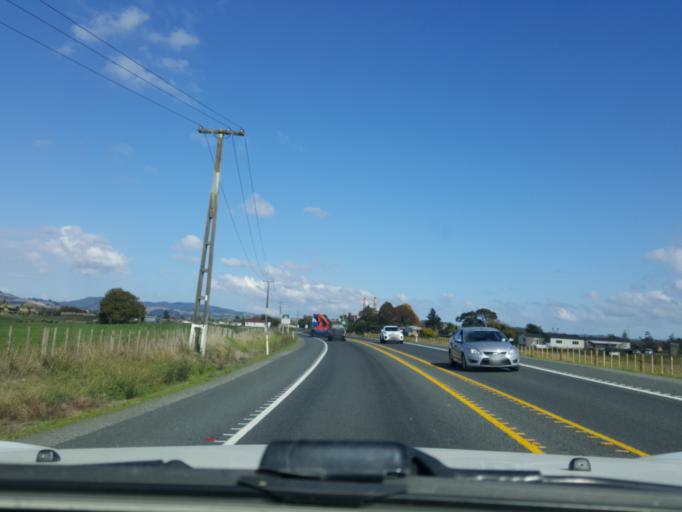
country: NZ
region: Waikato
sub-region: Waikato District
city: Te Kauwhata
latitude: -37.5186
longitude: 175.1632
